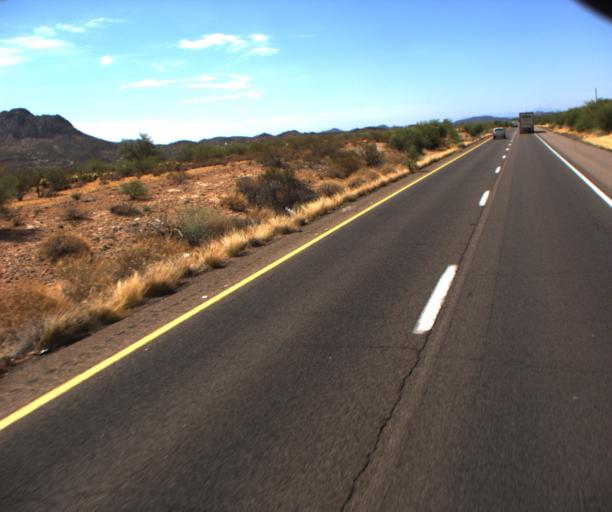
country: US
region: Arizona
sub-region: Maricopa County
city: New River
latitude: 33.9280
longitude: -112.1436
